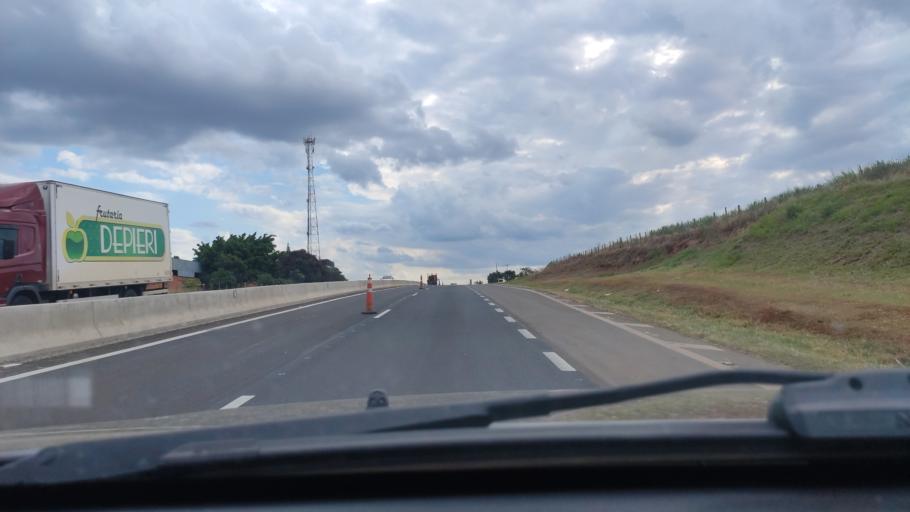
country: BR
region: Sao Paulo
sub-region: Santa Cruz Do Rio Pardo
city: Santa Cruz do Rio Pardo
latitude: -22.8681
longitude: -49.6231
